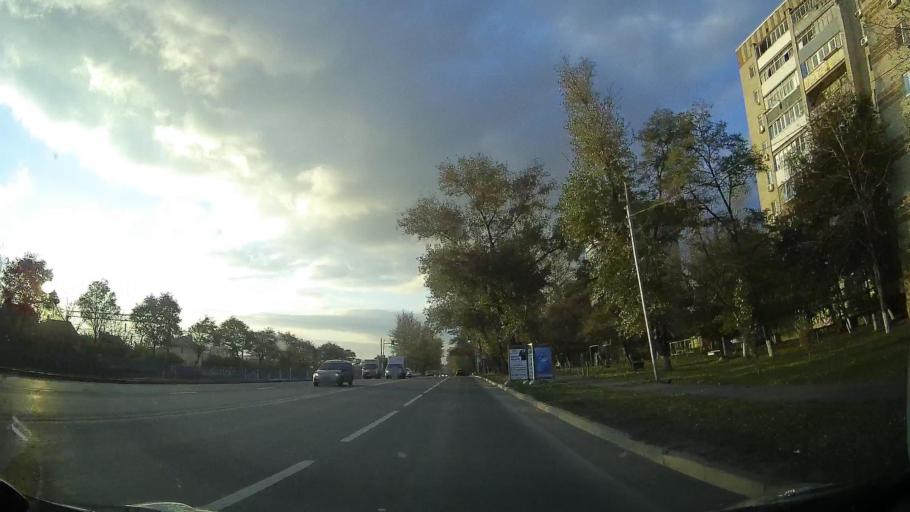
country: RU
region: Rostov
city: Imeni Chkalova
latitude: 47.2612
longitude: 39.7844
